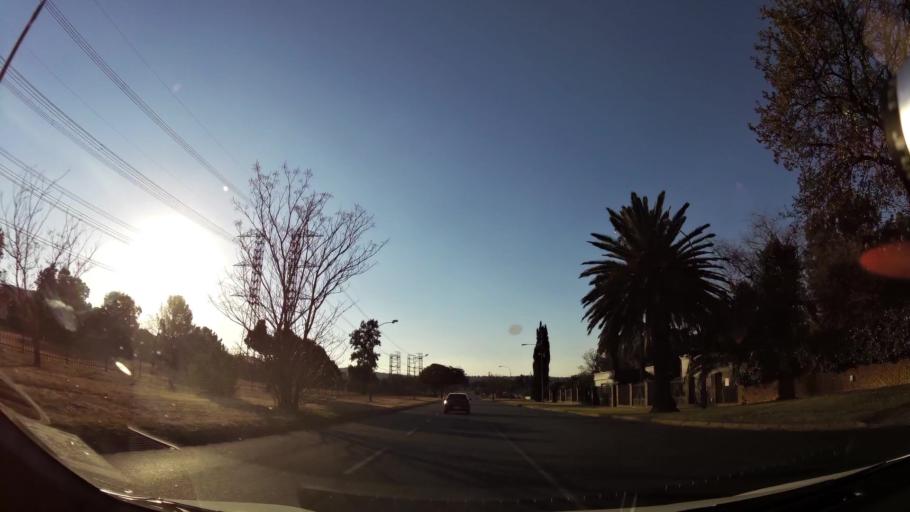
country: ZA
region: Gauteng
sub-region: Ekurhuleni Metropolitan Municipality
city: Germiston
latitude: -26.2774
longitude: 28.1093
